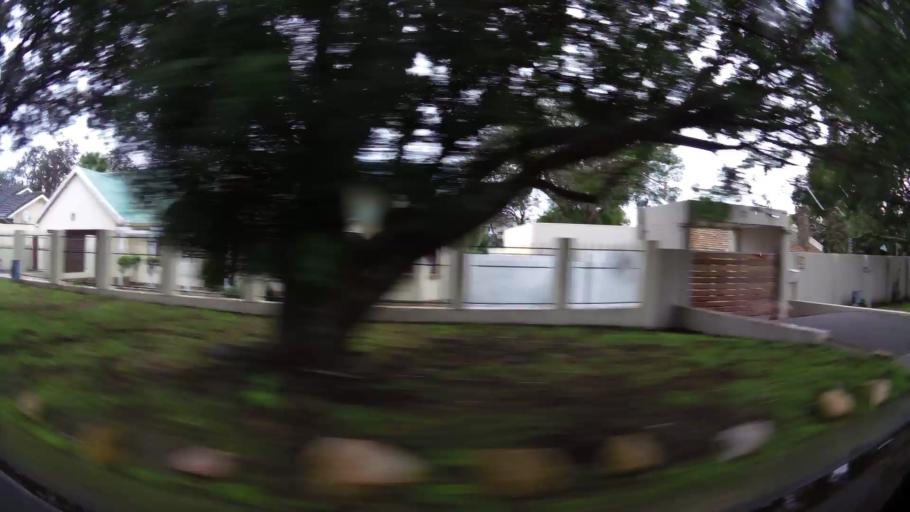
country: ZA
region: Eastern Cape
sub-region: Nelson Mandela Bay Metropolitan Municipality
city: Port Elizabeth
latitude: -33.9776
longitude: 25.5829
